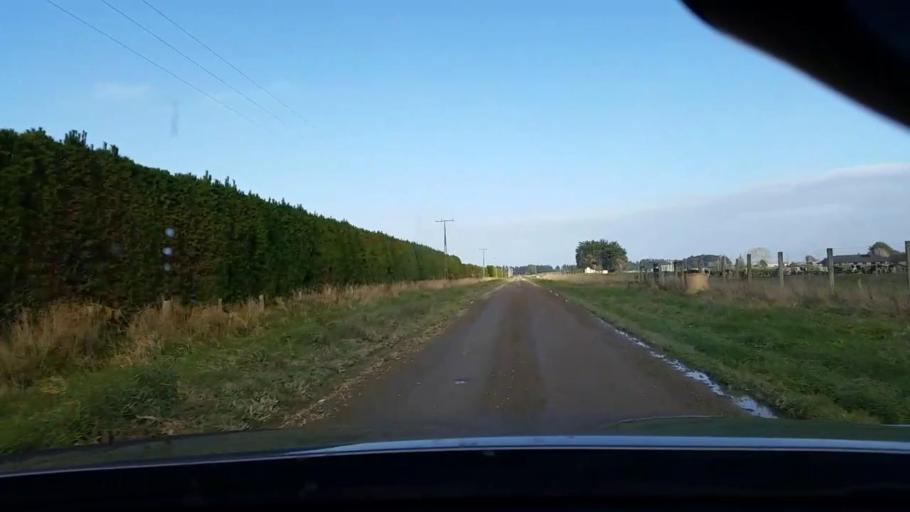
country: NZ
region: Southland
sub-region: Invercargill City
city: Invercargill
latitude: -46.2861
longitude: 168.2947
